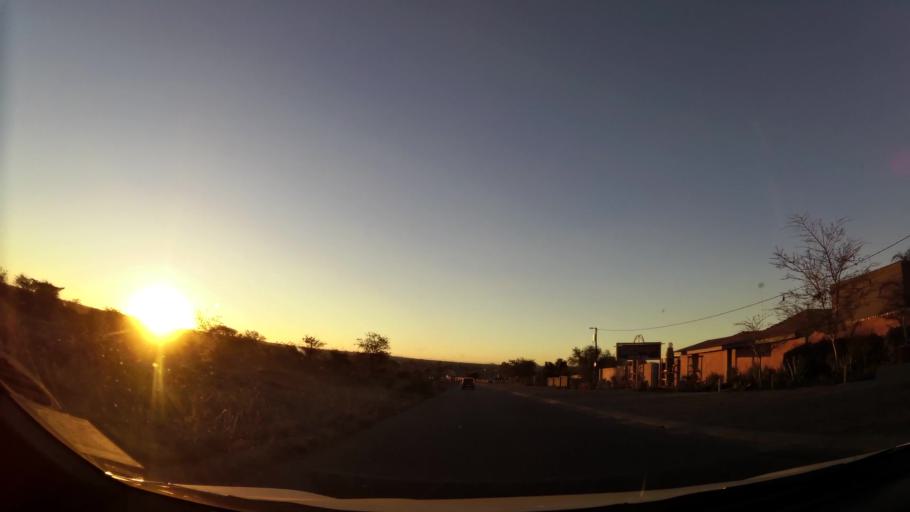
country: ZA
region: Limpopo
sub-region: Capricorn District Municipality
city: Polokwane
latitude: -23.8574
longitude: 29.3626
